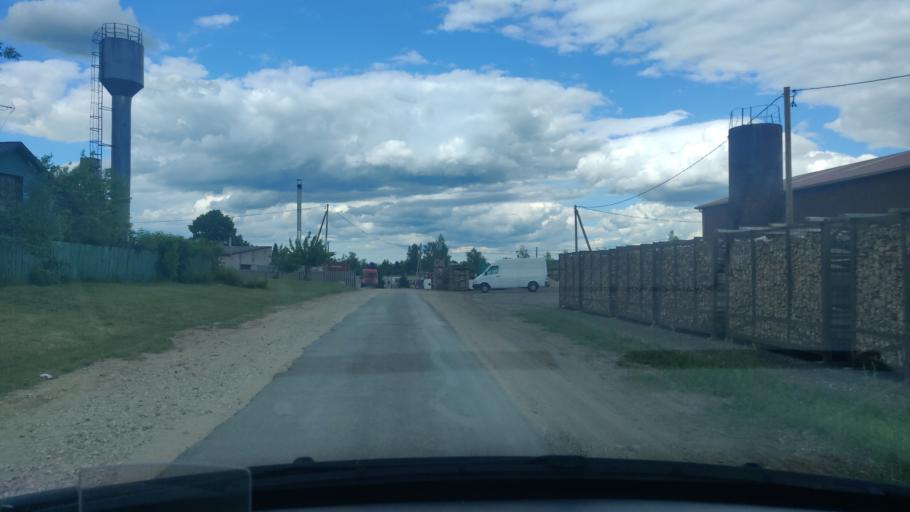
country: EE
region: Jogevamaa
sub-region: Mustvee linn
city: Mustvee
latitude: 58.9881
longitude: 26.8804
